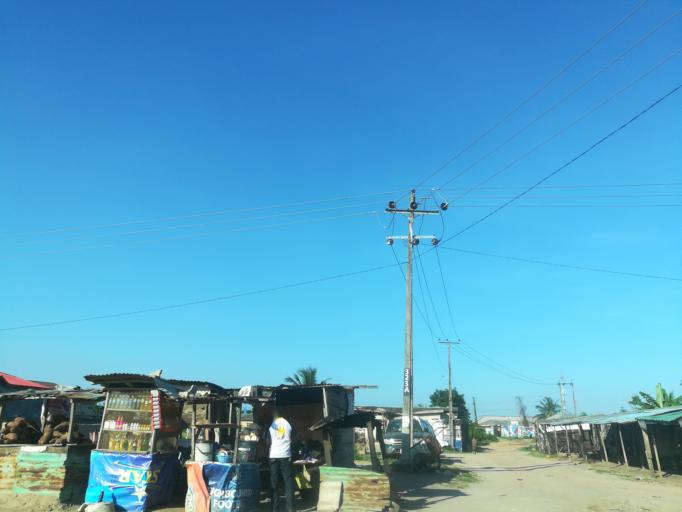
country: NG
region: Lagos
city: Ebute Ikorodu
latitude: 6.5473
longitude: 3.5424
